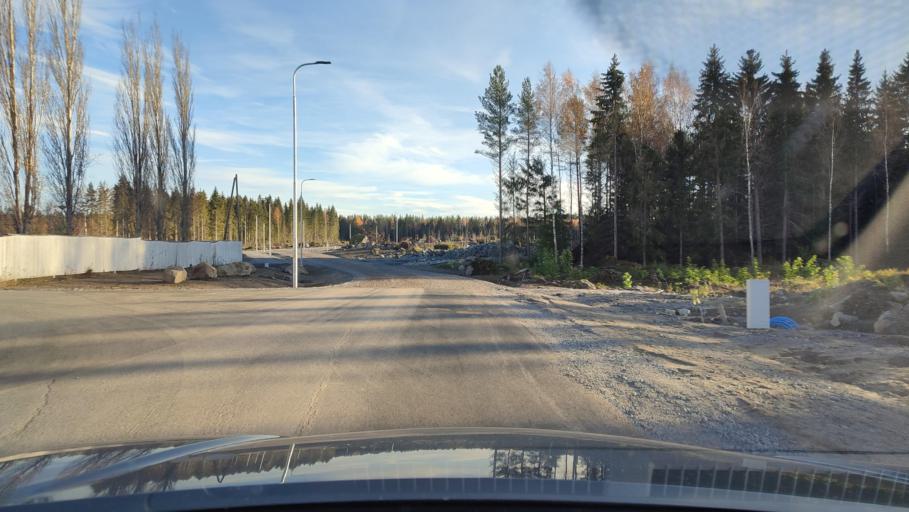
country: FI
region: Ostrobothnia
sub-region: Vaasa
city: Teeriniemi
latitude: 63.0654
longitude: 21.6997
